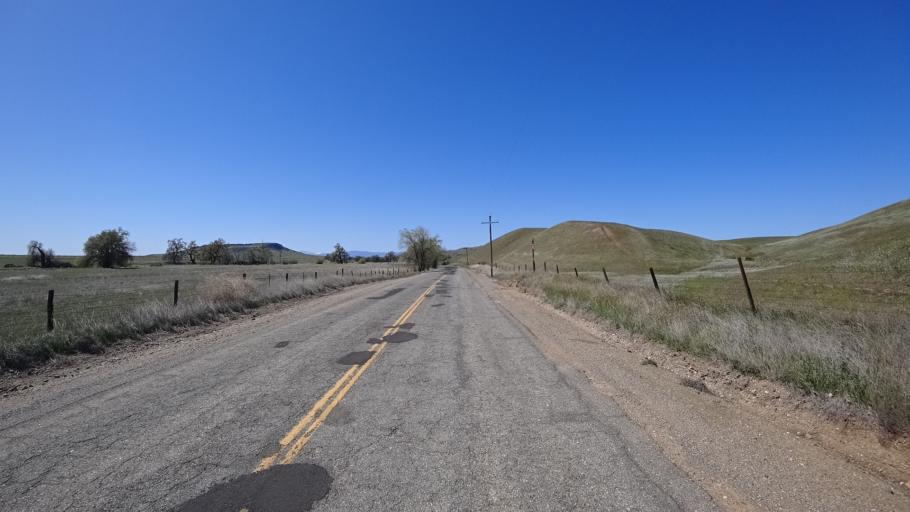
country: US
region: California
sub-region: Glenn County
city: Orland
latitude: 39.7798
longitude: -122.3076
